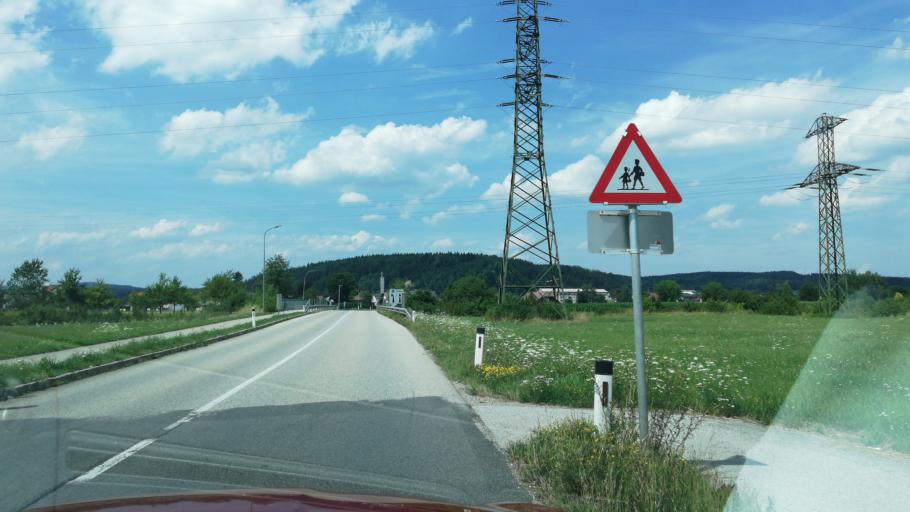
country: AT
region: Upper Austria
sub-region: Politischer Bezirk Vocklabruck
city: Timelkam
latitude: 47.9947
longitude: 13.6148
